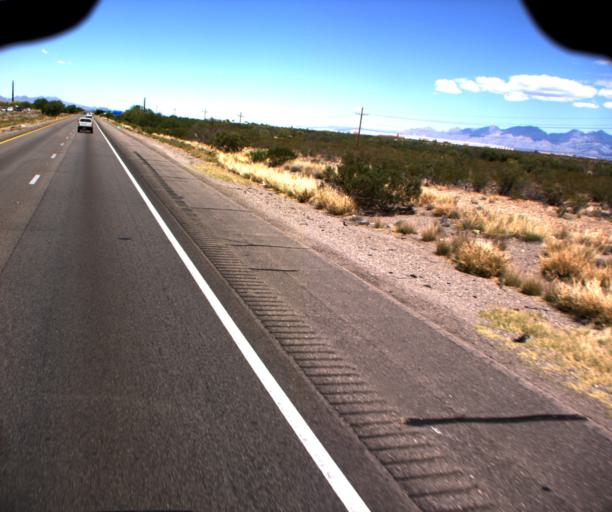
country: US
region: Arizona
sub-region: Pima County
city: Vail
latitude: 32.0726
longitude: -110.7909
